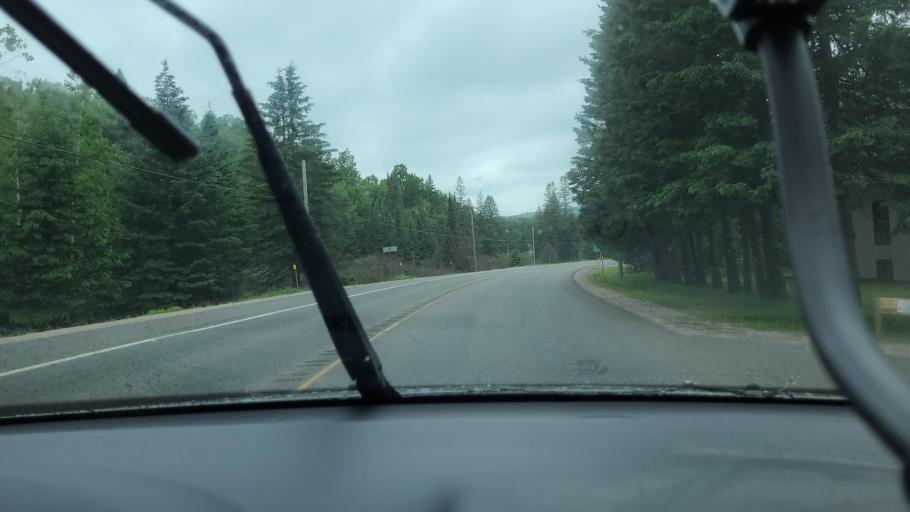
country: CA
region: Quebec
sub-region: Laurentides
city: Riviere-Rouge
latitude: 46.3698
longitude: -74.8441
